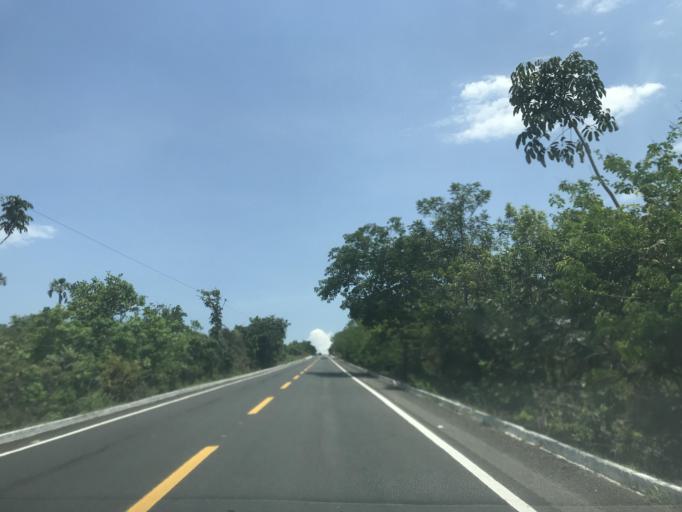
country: BR
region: Goias
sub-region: Bela Vista De Goias
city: Bela Vista de Goias
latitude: -17.1250
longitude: -48.6681
